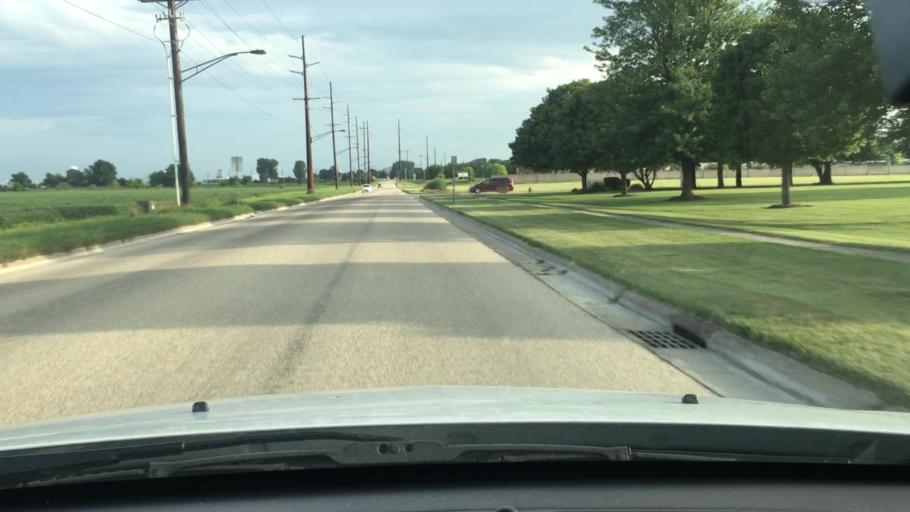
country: US
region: Illinois
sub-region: Ogle County
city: Rochelle
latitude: 41.9271
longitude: -89.0545
